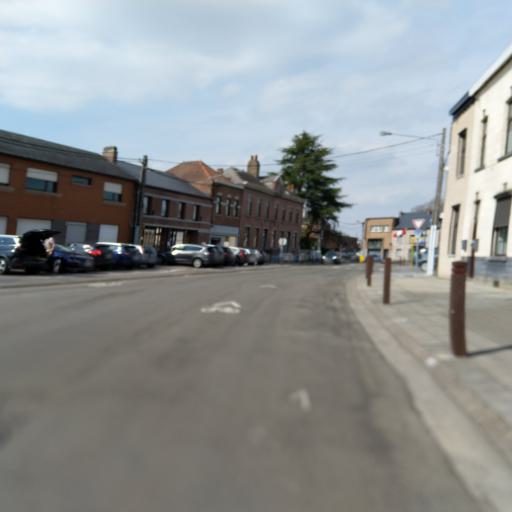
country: BE
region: Wallonia
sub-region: Province du Hainaut
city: Chasse Royale
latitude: 50.4387
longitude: 3.9612
